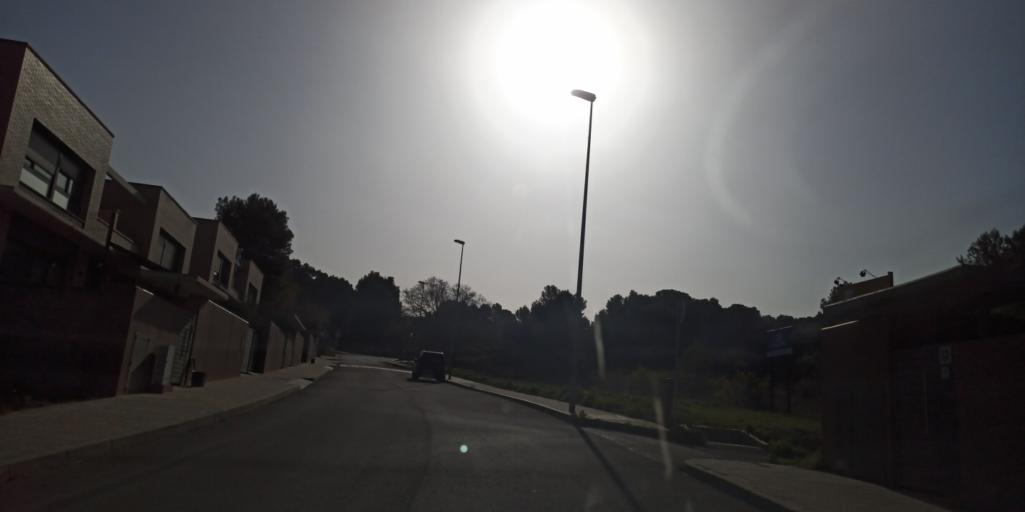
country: ES
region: Catalonia
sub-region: Provincia de Barcelona
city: Castelloli
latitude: 41.5987
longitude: 1.7050
